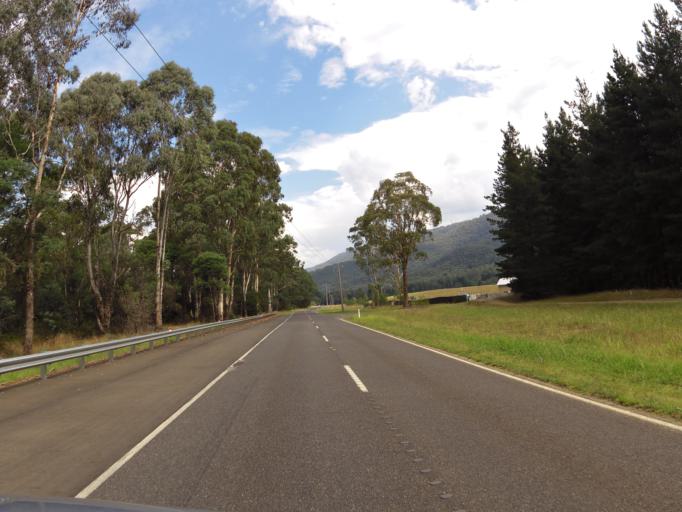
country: AU
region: Victoria
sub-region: Alpine
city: Mount Beauty
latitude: -36.7591
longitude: 147.0230
